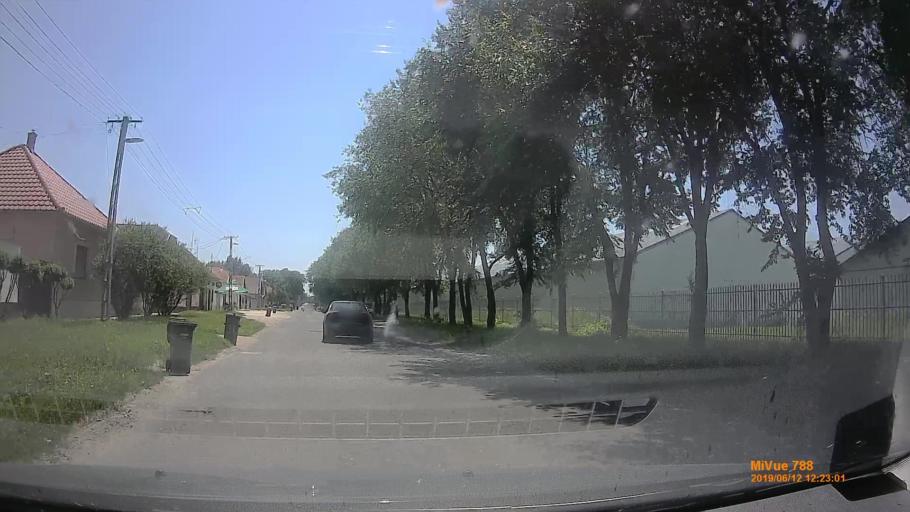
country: HU
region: Bacs-Kiskun
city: Kecskemet
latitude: 46.8948
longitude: 19.6997
